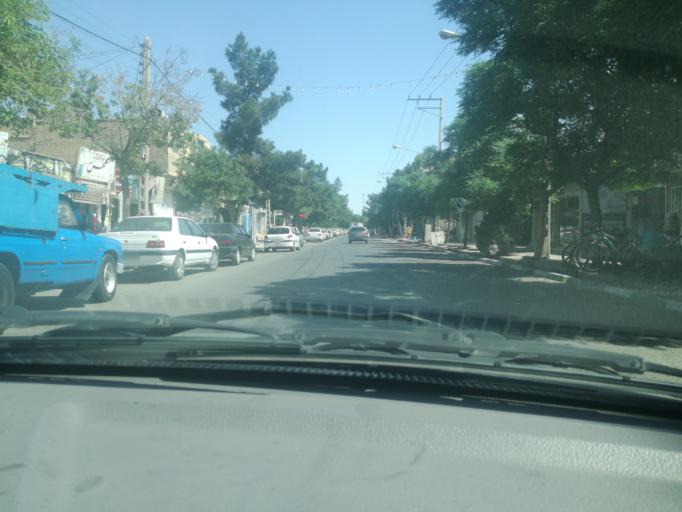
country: IR
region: Razavi Khorasan
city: Sarakhs
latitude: 36.5396
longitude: 61.1636
